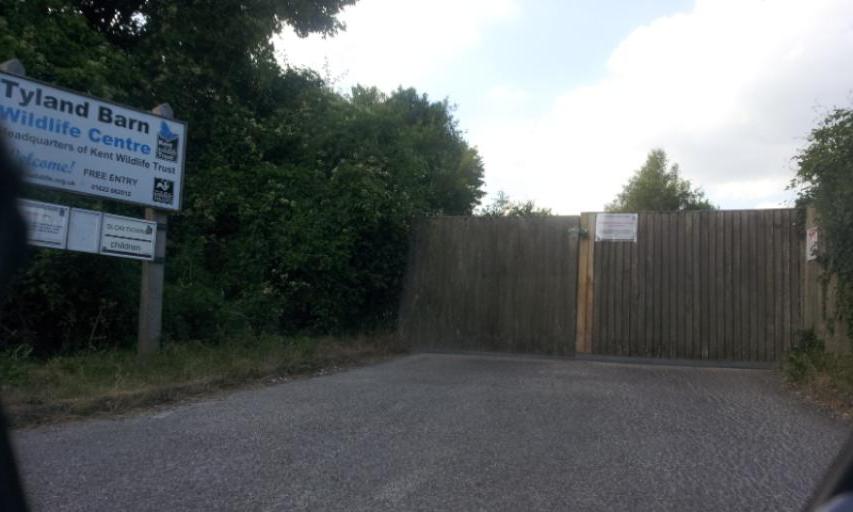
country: GB
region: England
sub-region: Kent
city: Boxley
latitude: 51.3055
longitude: 0.5133
